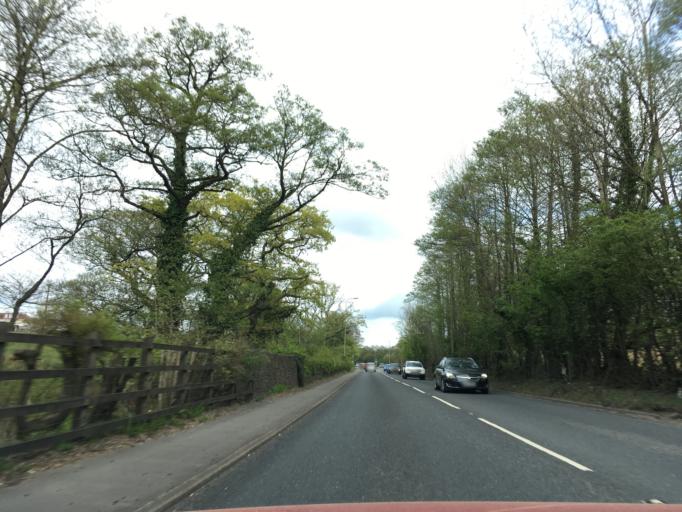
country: GB
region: Wales
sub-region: Caerphilly County Borough
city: Nelson
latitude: 51.6479
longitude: -3.2978
